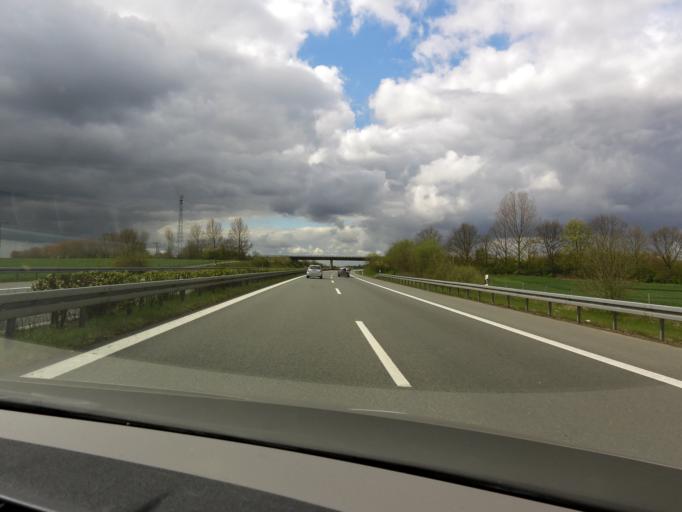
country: DE
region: Mecklenburg-Vorpommern
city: Bad Sulze
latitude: 54.0301
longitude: 12.5977
